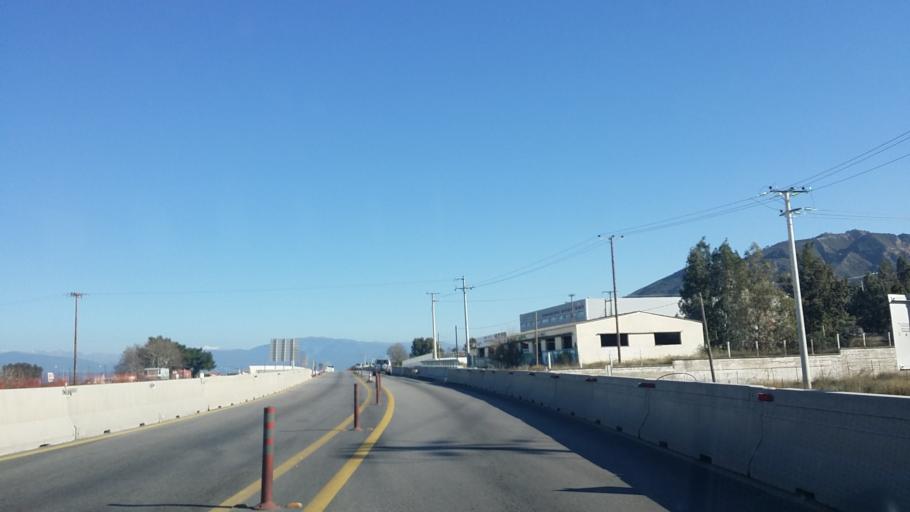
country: GR
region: West Greece
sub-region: Nomos Achaias
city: Rio
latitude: 38.3048
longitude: 21.8048
